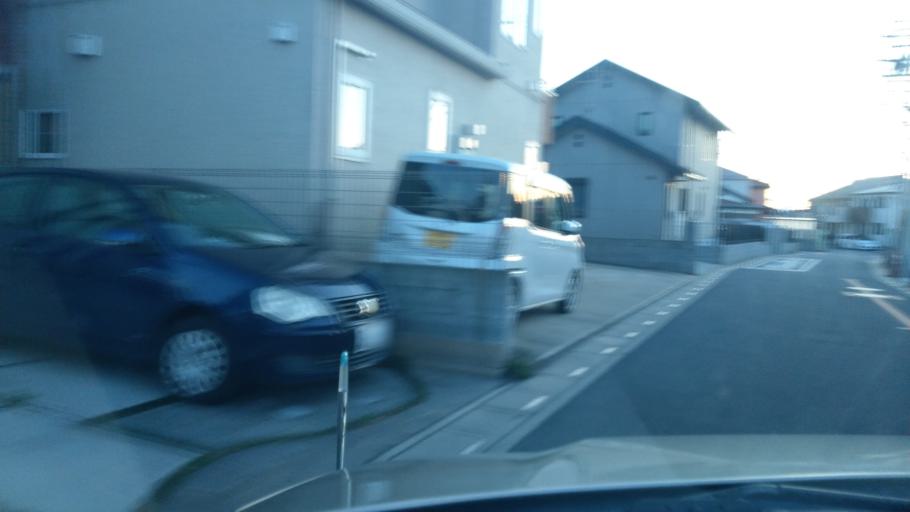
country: JP
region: Saitama
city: Ageoshimo
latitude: 35.9216
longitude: 139.5769
